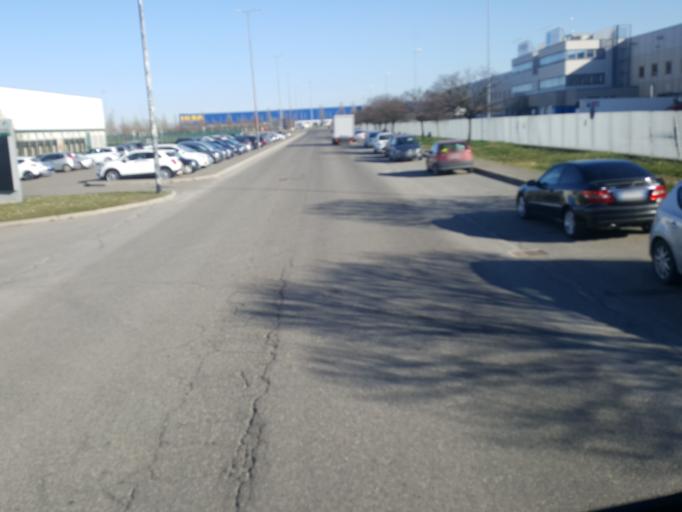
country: IT
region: Emilia-Romagna
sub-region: Provincia di Piacenza
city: Pontenure
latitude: 45.0315
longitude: 9.7575
